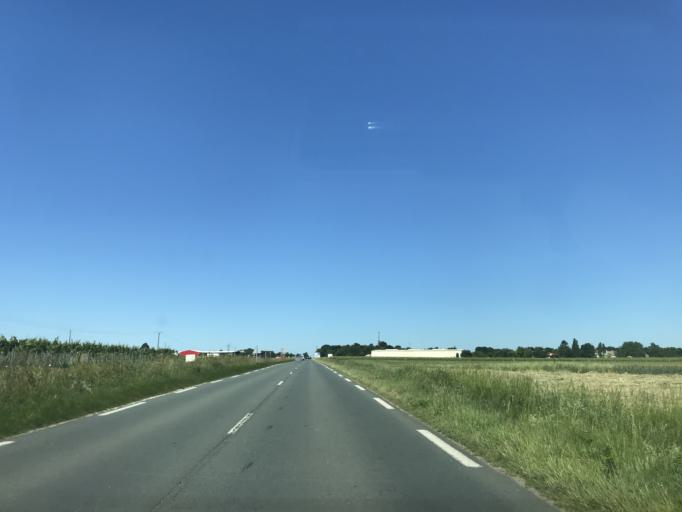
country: FR
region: Poitou-Charentes
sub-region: Departement de la Charente-Maritime
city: Pons
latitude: 45.5731
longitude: -0.5855
